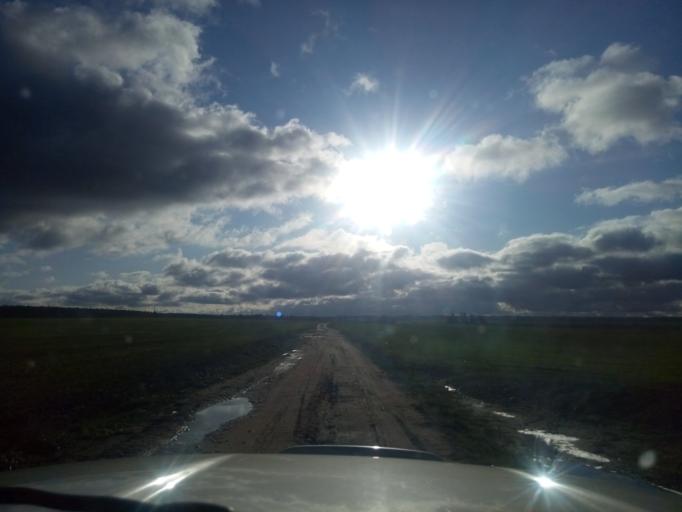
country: BY
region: Minsk
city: Tsimkavichy
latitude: 53.1929
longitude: 26.9035
